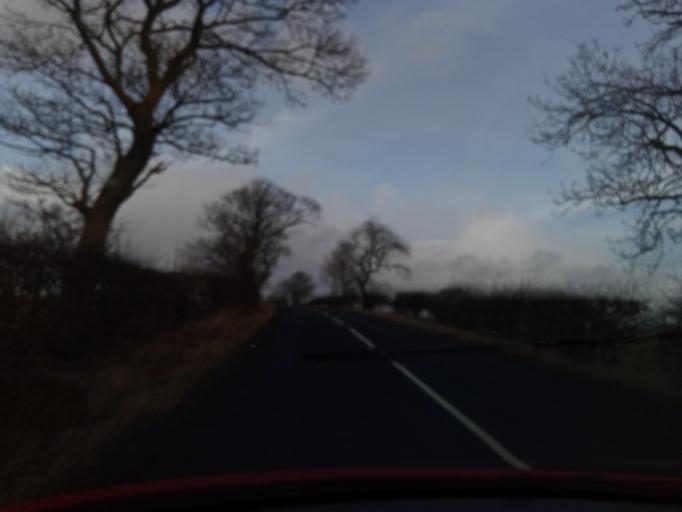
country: GB
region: England
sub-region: Northumberland
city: Acomb
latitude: 55.0885
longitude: -2.0603
